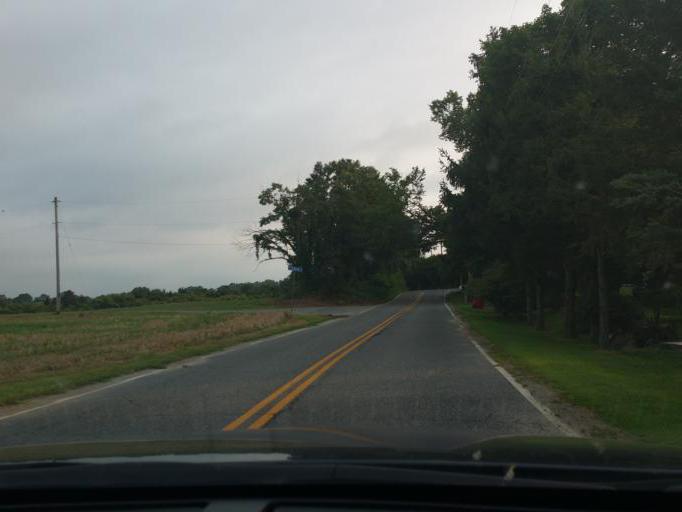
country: US
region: Maryland
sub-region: Cecil County
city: Rising Sun
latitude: 39.7180
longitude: -76.2013
